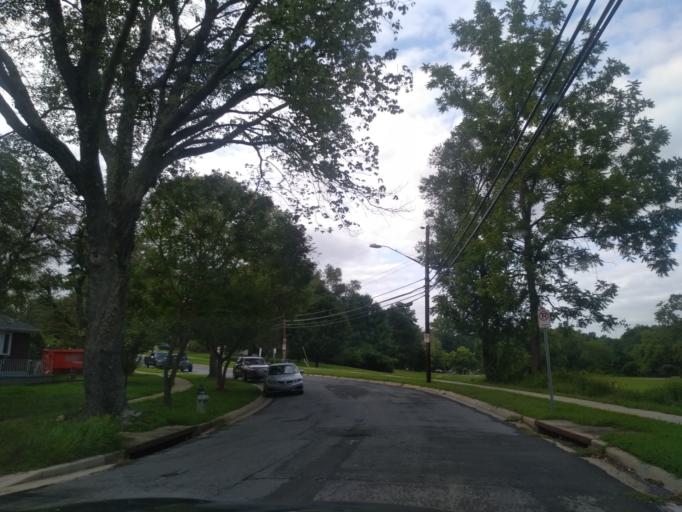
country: US
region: Maryland
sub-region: Montgomery County
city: North Kensington
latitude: 39.0465
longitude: -77.0919
